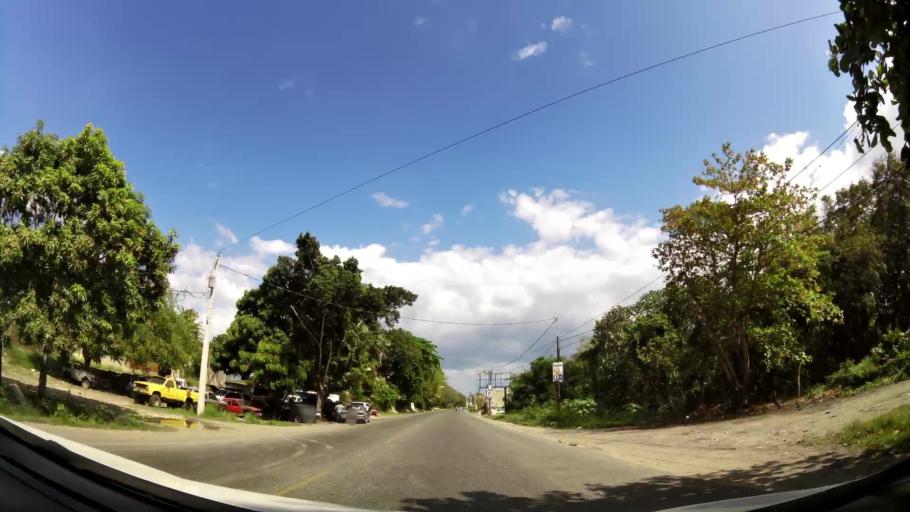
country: DO
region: San Cristobal
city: San Cristobal
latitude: 18.4274
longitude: -70.0781
